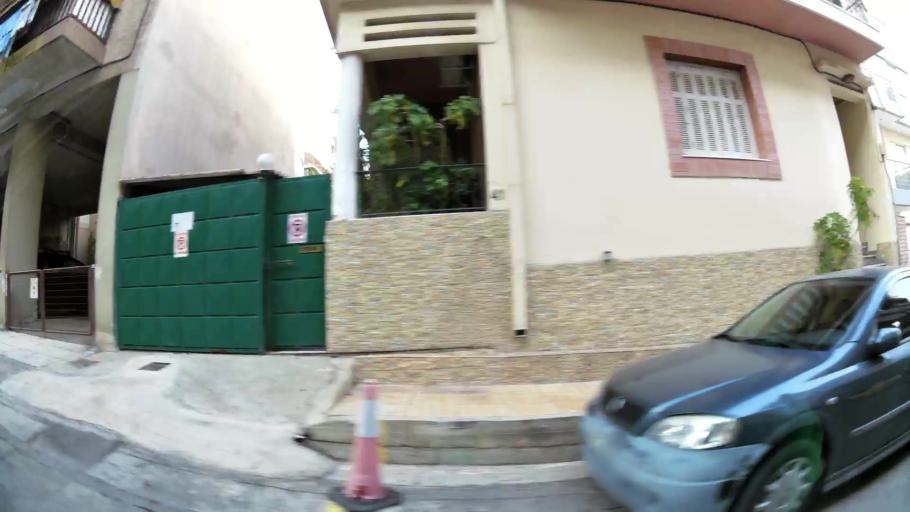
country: GR
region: Attica
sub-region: Nomarchia Athinas
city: Galatsi
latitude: 38.0245
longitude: 23.7525
